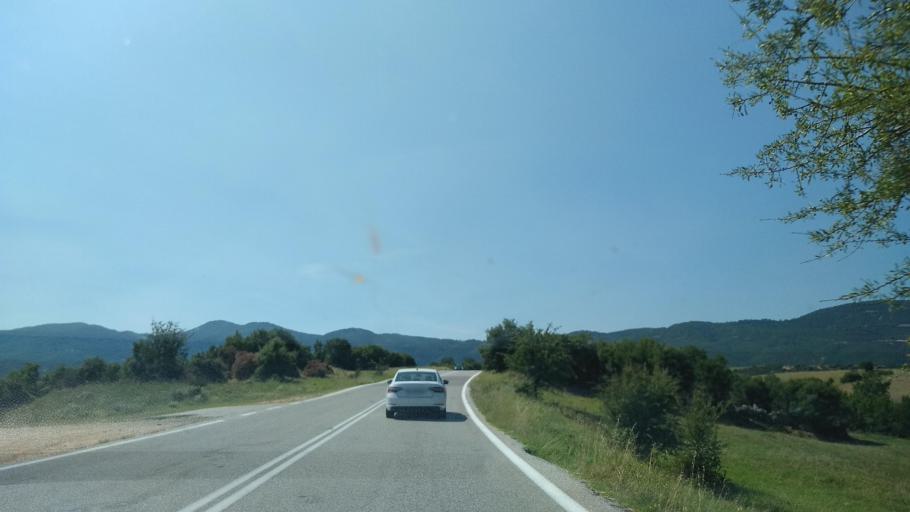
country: GR
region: Central Macedonia
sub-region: Nomos Thessalonikis
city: Nea Apollonia
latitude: 40.5173
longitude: 23.4729
